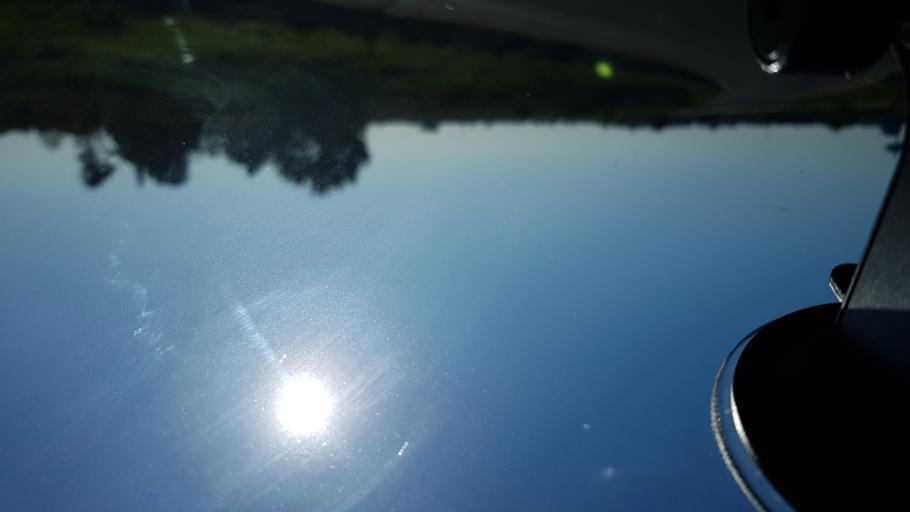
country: IT
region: Apulia
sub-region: Provincia di Lecce
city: Merine
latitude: 40.4094
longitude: 18.2580
